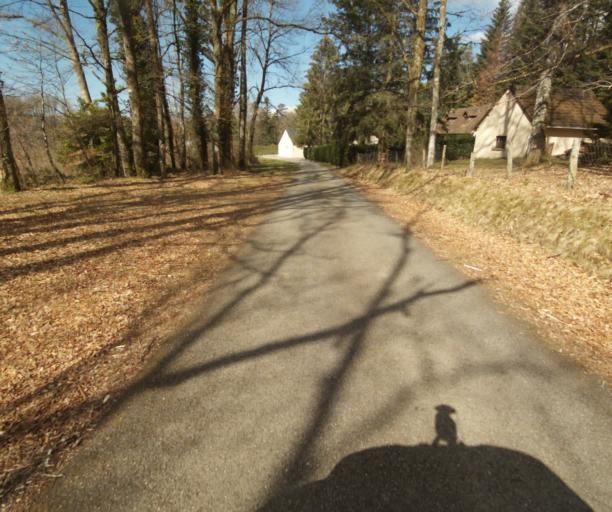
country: FR
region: Limousin
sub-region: Departement de la Correze
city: Argentat
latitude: 45.2311
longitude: 1.9177
